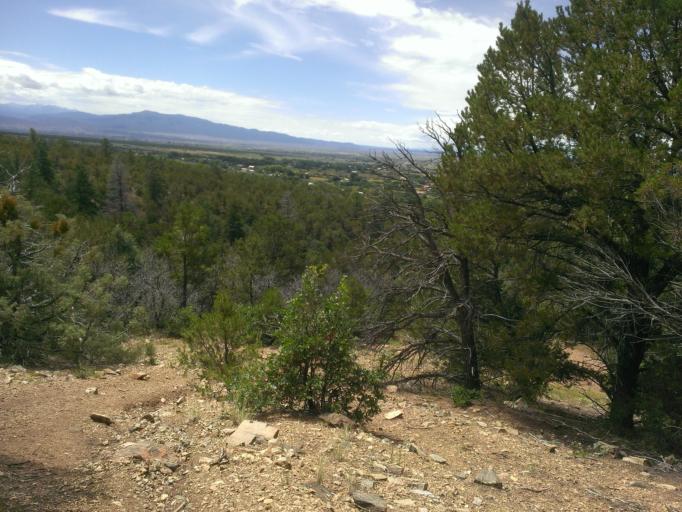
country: US
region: New Mexico
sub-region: Taos County
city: Arroyo Seco
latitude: 36.5363
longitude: -105.5562
